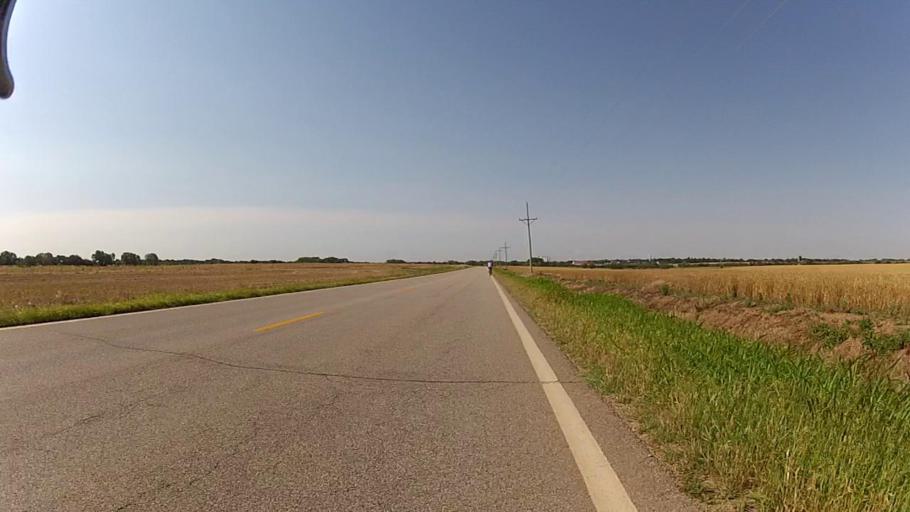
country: US
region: Kansas
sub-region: Sumner County
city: Caldwell
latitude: 37.0546
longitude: -97.6008
